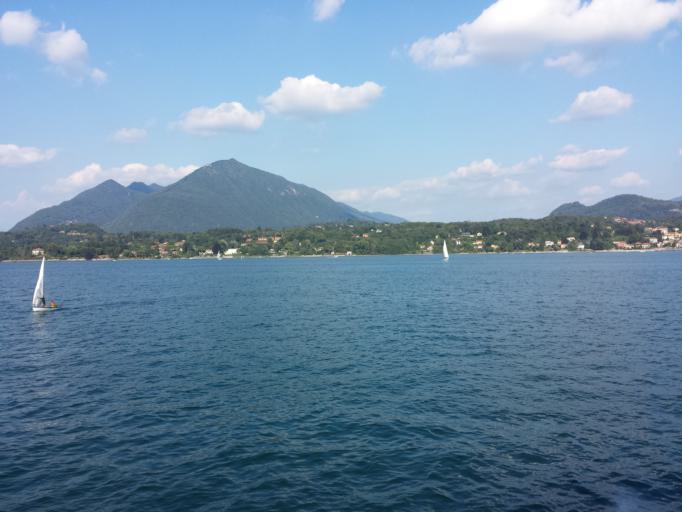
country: IT
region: Lombardy
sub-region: Provincia di Varese
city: Leggiuno
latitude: 45.8823
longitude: 8.5813
